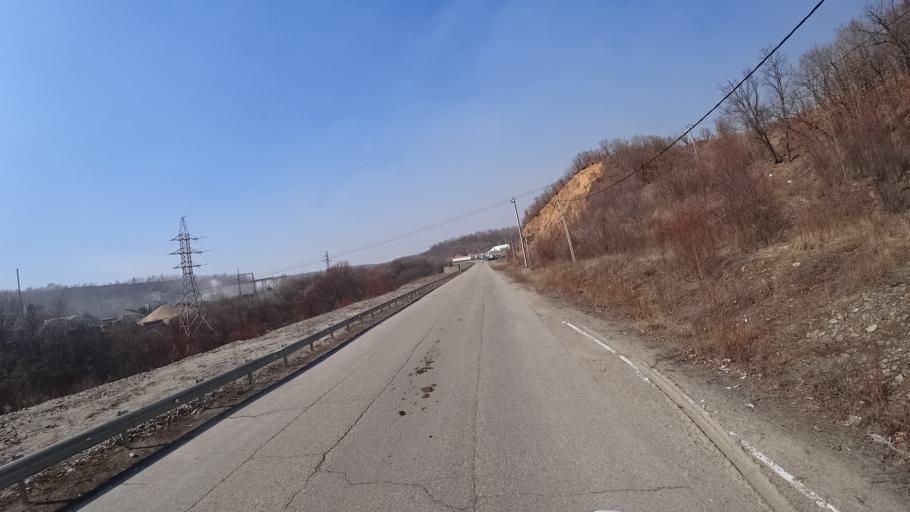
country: RU
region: Amur
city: Novobureyskiy
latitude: 49.7907
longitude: 129.9652
